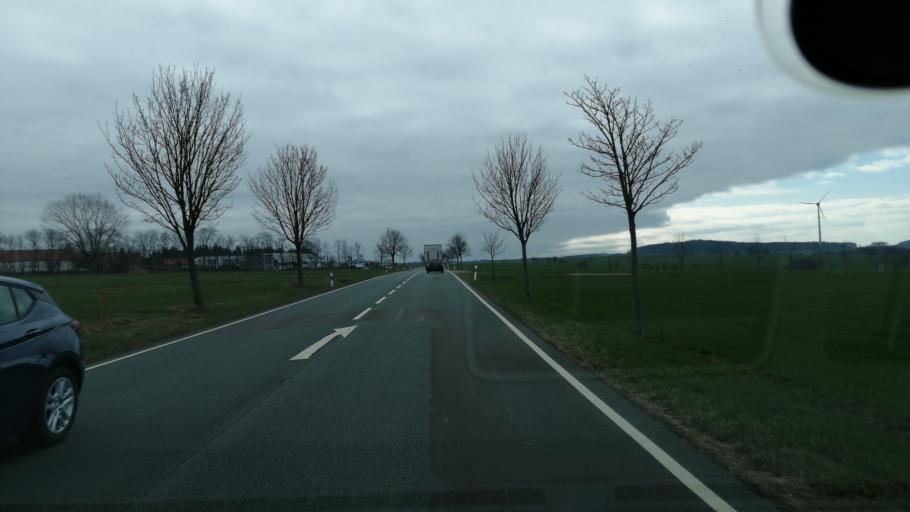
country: DE
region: Saxony
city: Lobau
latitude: 51.0778
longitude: 14.6768
